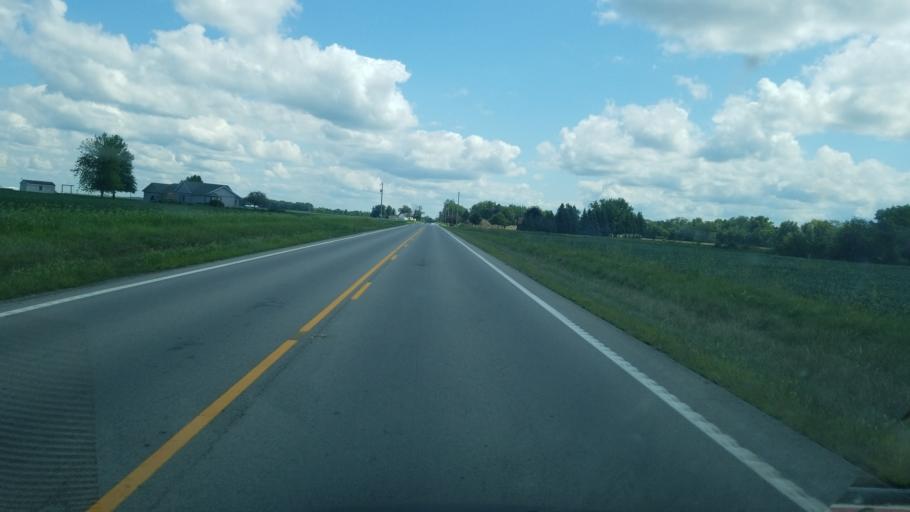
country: US
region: Ohio
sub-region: Putnam County
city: Kalida
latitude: 40.9536
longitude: -84.1699
